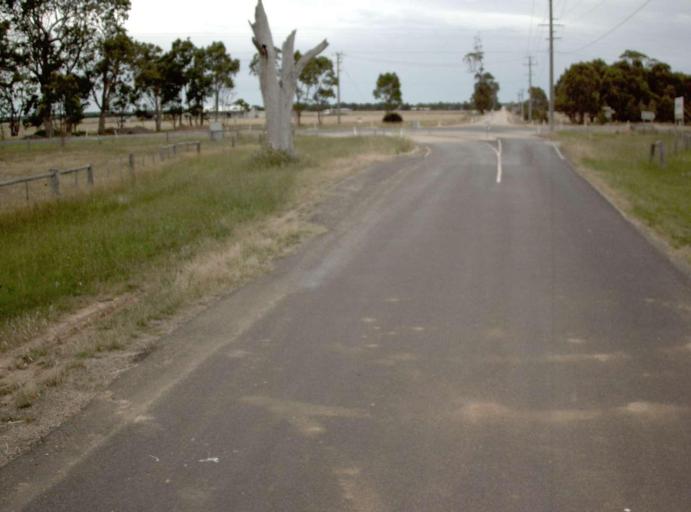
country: AU
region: Victoria
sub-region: East Gippsland
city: Bairnsdale
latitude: -37.8466
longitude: 147.5665
